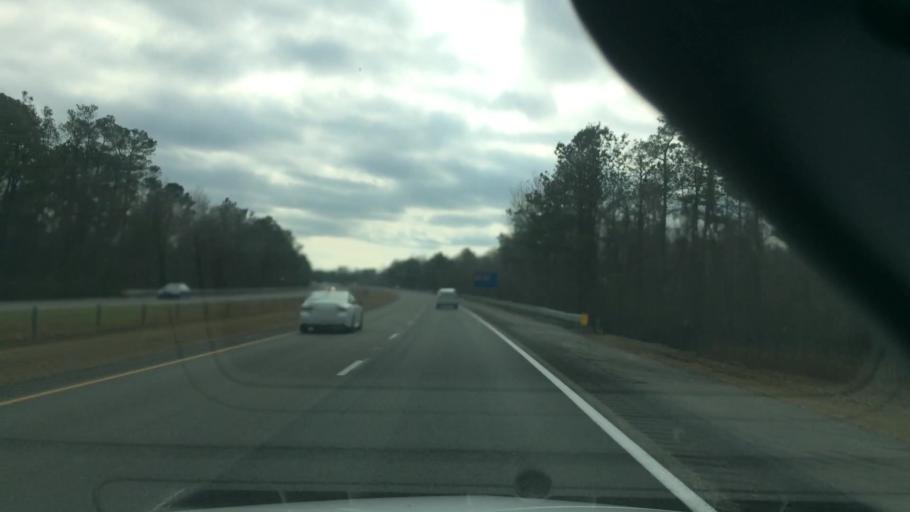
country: US
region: North Carolina
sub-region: New Hanover County
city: Castle Hayne
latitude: 34.3710
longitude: -77.8872
